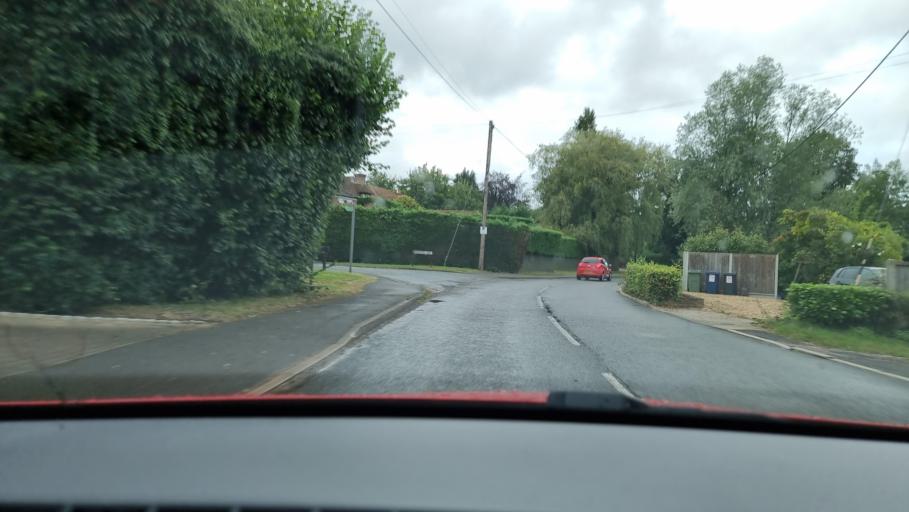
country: GB
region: England
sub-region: Hertfordshire
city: Berkhamsted
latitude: 51.7352
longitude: -0.5851
